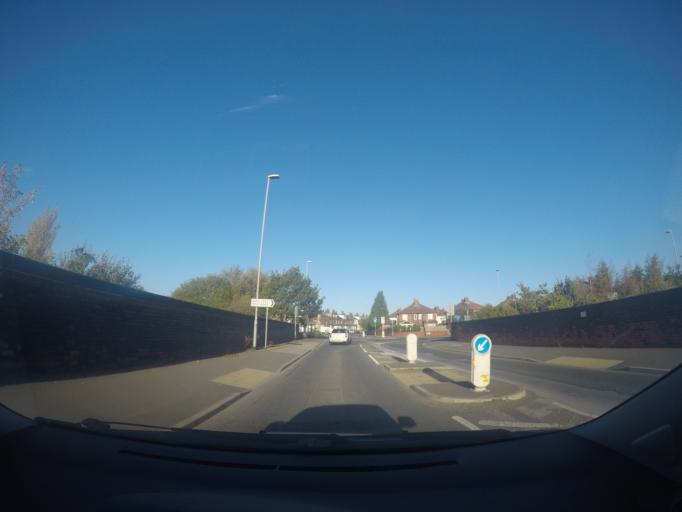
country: GB
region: England
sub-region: City and Borough of Leeds
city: Leeds
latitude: 53.7910
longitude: -1.5137
